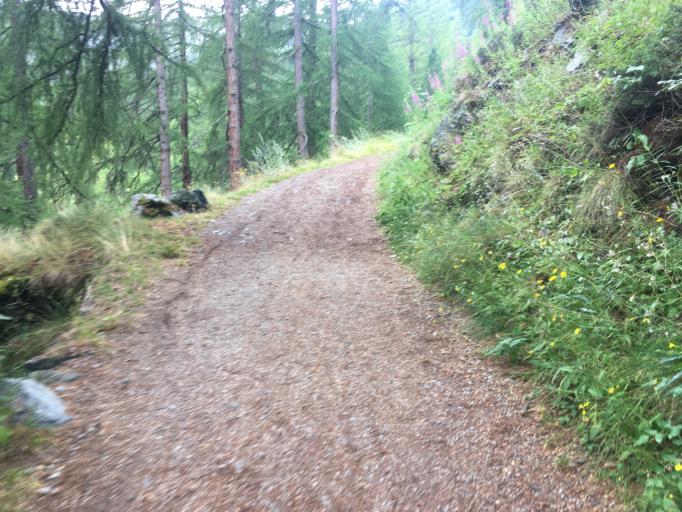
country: CH
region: Valais
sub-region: Visp District
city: Zermatt
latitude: 46.0096
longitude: 7.7313
